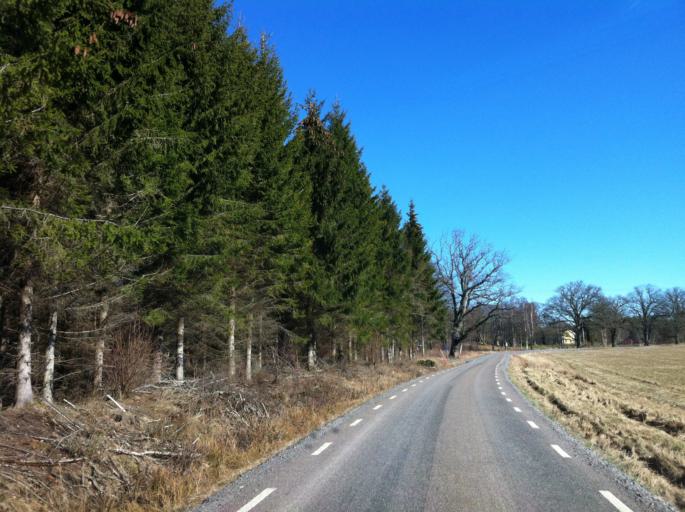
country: SE
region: Vaestra Goetaland
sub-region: Grastorps Kommun
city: Graestorp
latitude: 58.4379
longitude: 12.6089
